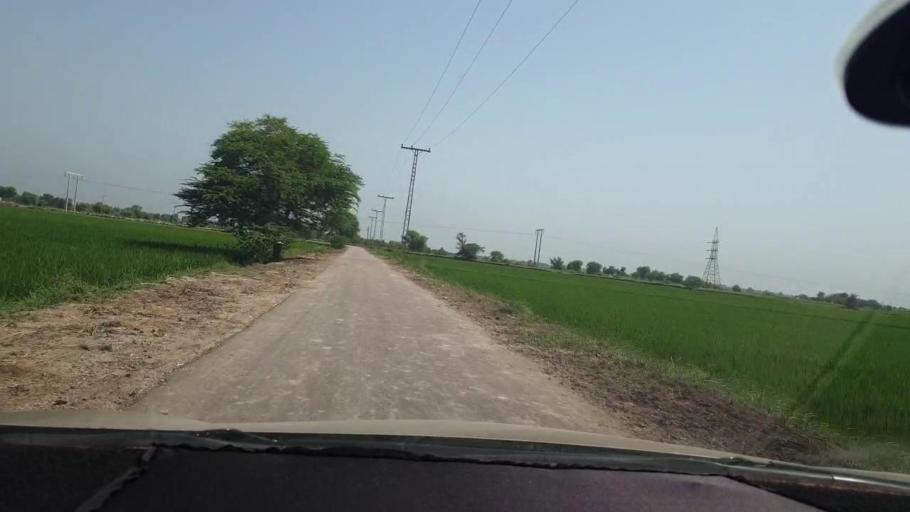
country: PK
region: Sindh
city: Kambar
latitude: 27.5007
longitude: 68.0170
